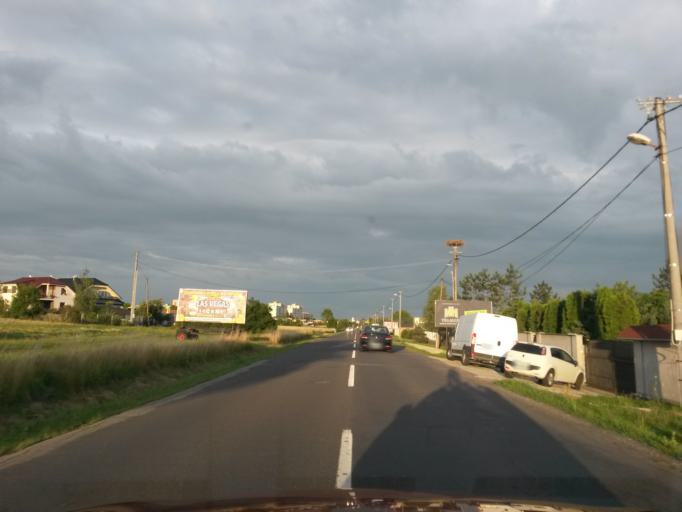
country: SK
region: Banskobystricky
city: Lucenec
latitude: 48.3355
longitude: 19.6295
